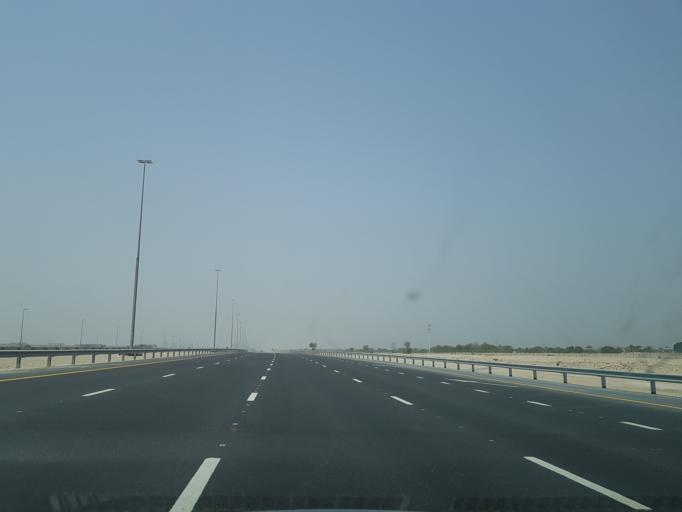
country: AE
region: Dubai
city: Dubai
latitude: 25.0527
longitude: 55.2912
